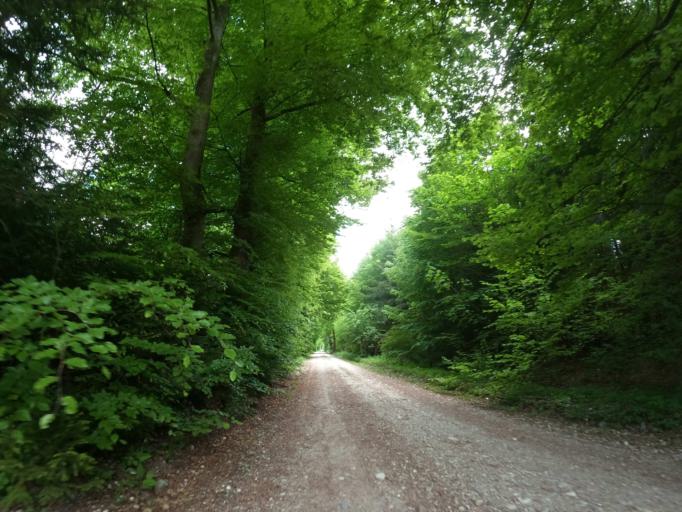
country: DE
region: Bavaria
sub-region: Upper Bavaria
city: Brunnthal
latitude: 47.9737
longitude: 11.7031
